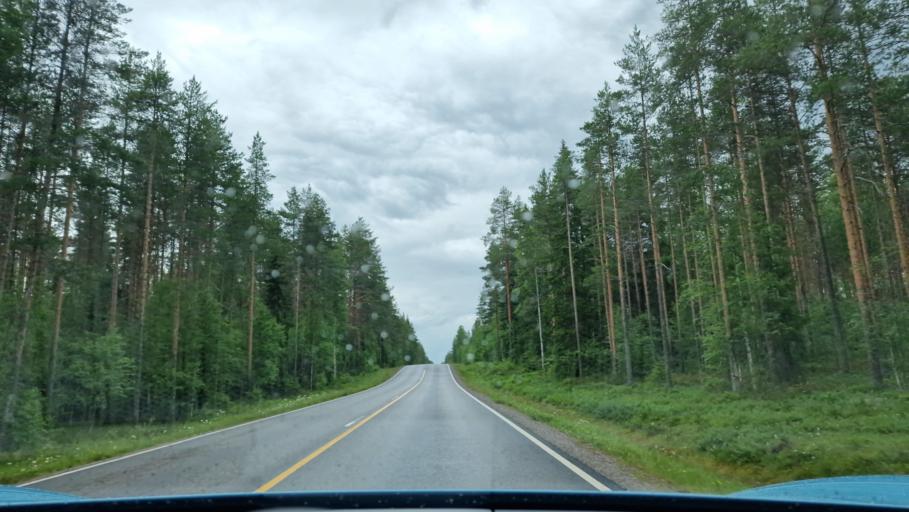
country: FI
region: Central Finland
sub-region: Saarijaervi-Viitasaari
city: Pylkoenmaeki
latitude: 62.6254
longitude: 24.5802
